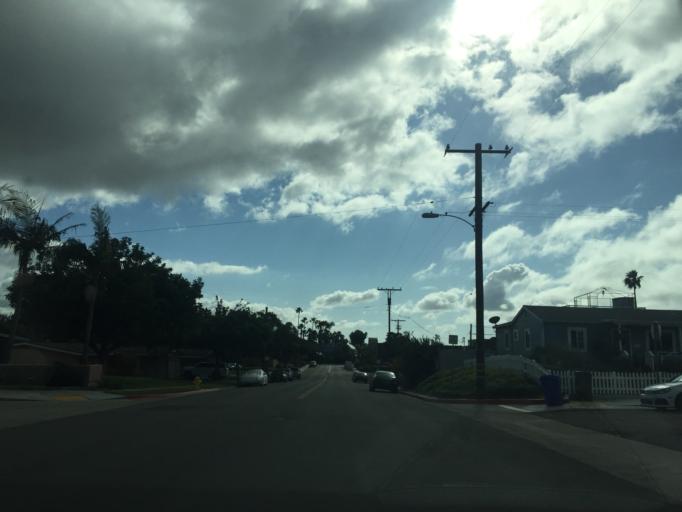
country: US
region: California
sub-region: San Diego County
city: La Jolla
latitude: 32.7985
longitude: -117.2288
